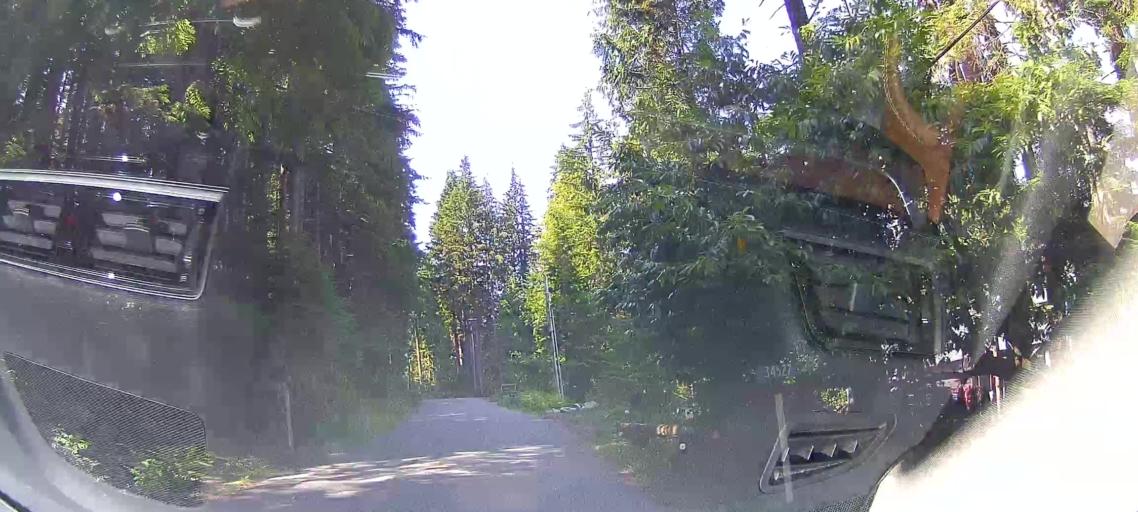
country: US
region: Washington
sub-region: Snohomish County
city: Arlington Heights
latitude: 48.3132
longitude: -121.9986
